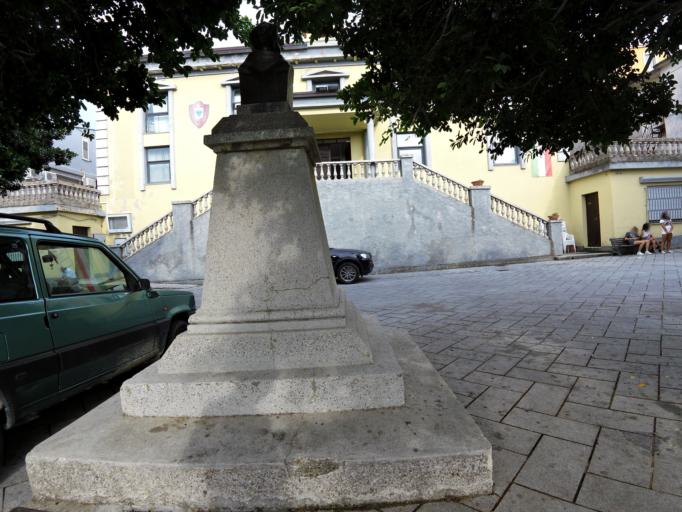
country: IT
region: Calabria
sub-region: Provincia di Reggio Calabria
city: Stignano
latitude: 38.4183
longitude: 16.4703
